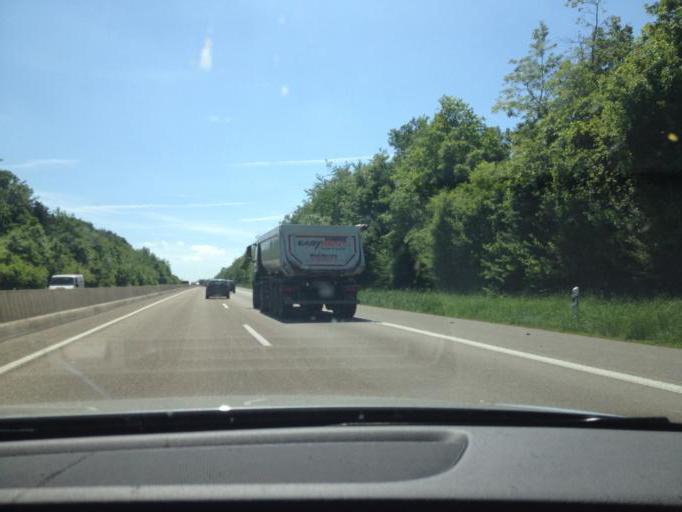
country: DE
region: North Rhine-Westphalia
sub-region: Regierungsbezirk Koln
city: Euskirchen
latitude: 50.6377
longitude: 6.7206
